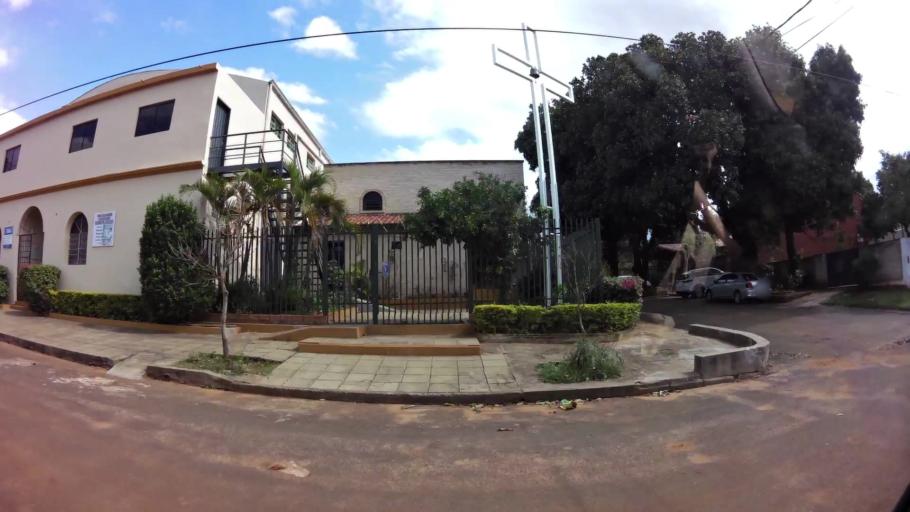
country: PY
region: Central
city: San Lorenzo
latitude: -25.2675
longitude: -57.5033
